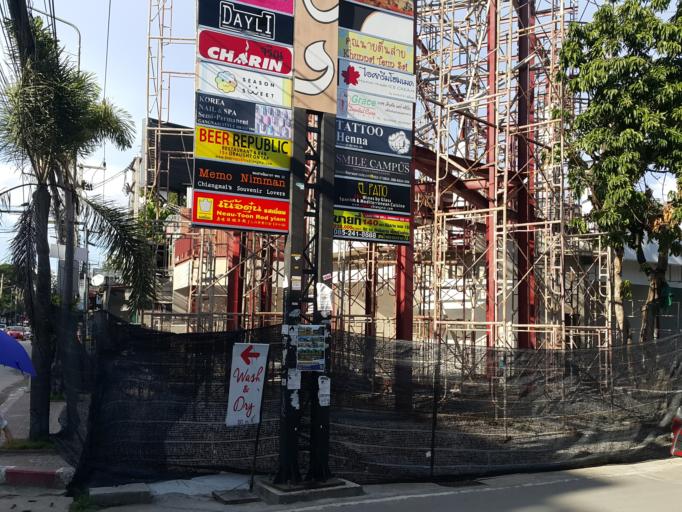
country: TH
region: Chiang Mai
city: Chiang Mai
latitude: 18.7971
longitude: 98.9664
